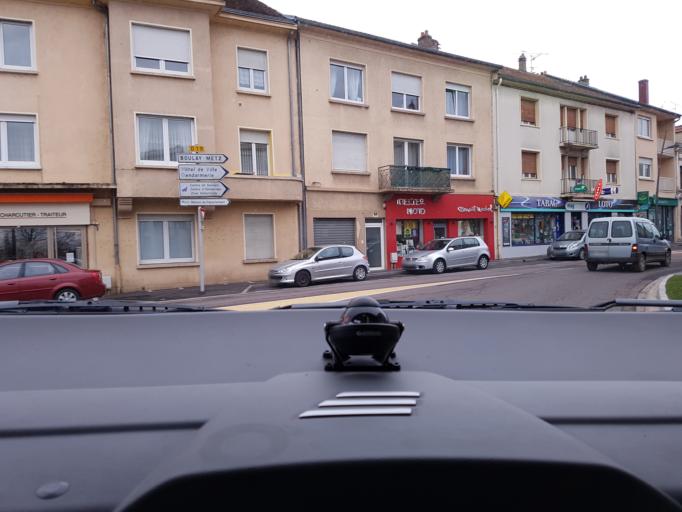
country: FR
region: Lorraine
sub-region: Departement de la Moselle
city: Faulquemont
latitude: 49.0420
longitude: 6.5995
